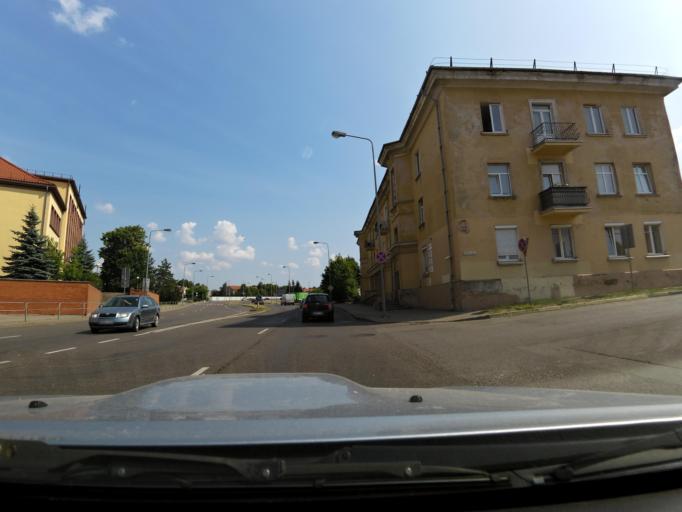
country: LT
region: Klaipedos apskritis
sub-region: Klaipeda
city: Klaipeda
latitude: 55.7206
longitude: 21.1223
